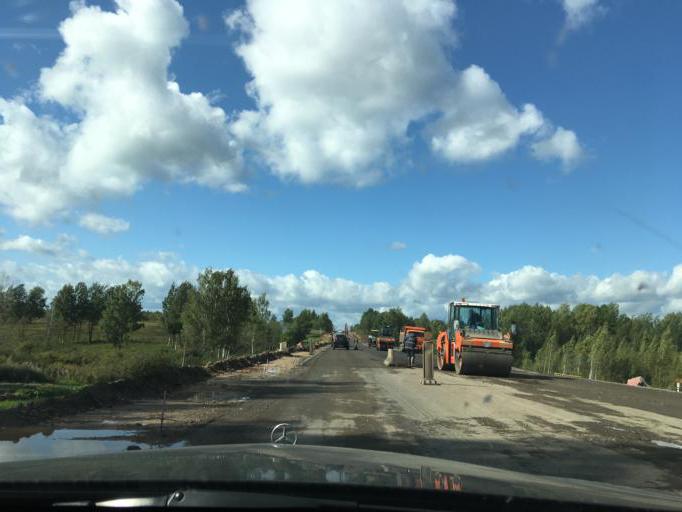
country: RU
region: Pskov
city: Velikiye Luki
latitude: 56.2701
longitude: 30.3785
